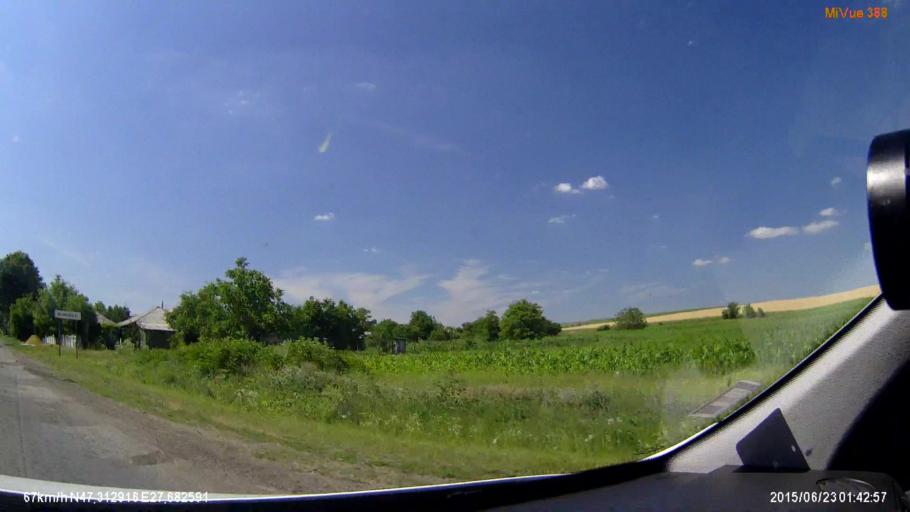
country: RO
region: Iasi
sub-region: Comuna Golaesti
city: Golaesti
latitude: 47.3128
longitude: 27.6828
